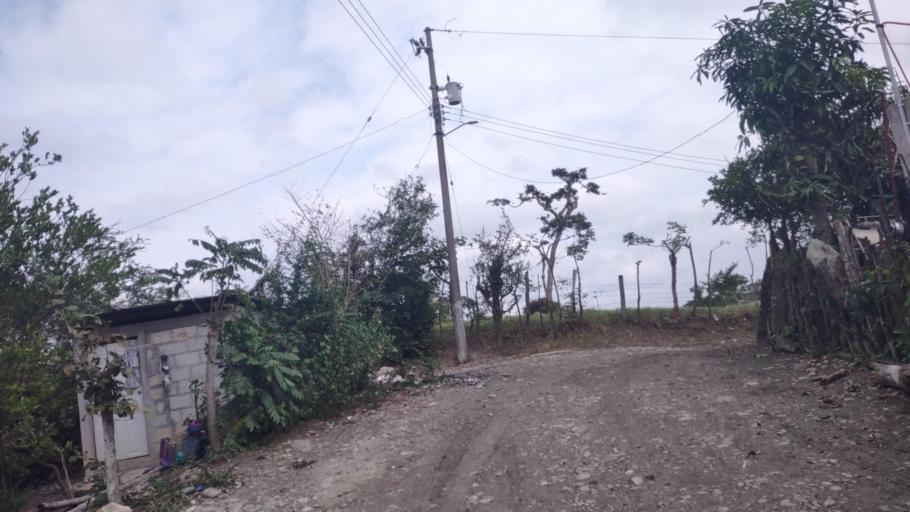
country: MX
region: Veracruz
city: Coatzintla
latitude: 20.4598
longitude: -97.4193
